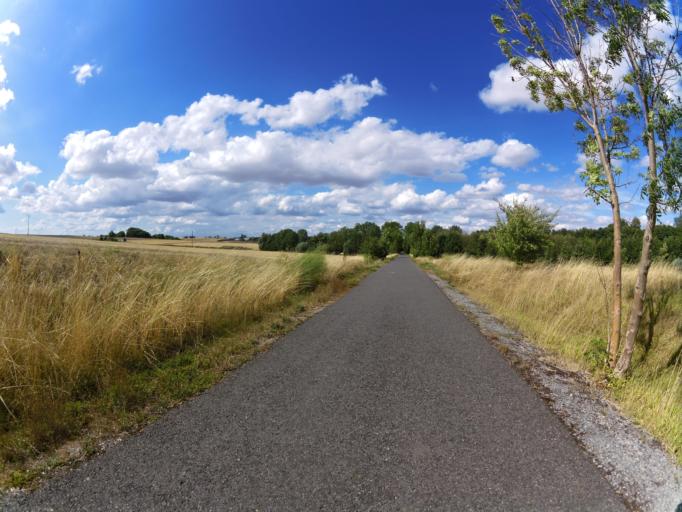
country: DE
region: Bavaria
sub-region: Regierungsbezirk Unterfranken
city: Gaukonigshofen
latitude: 49.6231
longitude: 10.0097
